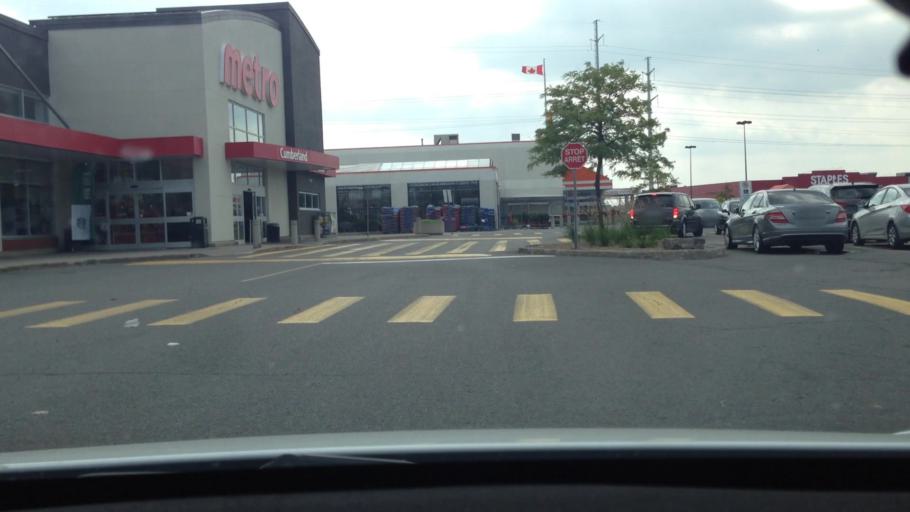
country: CA
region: Ontario
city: Clarence-Rockland
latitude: 45.4613
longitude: -75.4847
